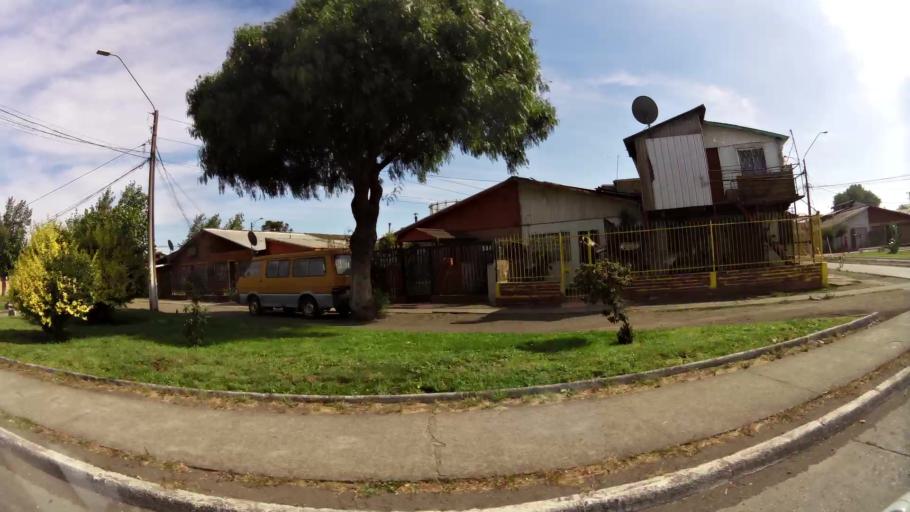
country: CL
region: Biobio
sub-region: Provincia de Concepcion
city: Talcahuano
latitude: -36.7782
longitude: -73.1111
